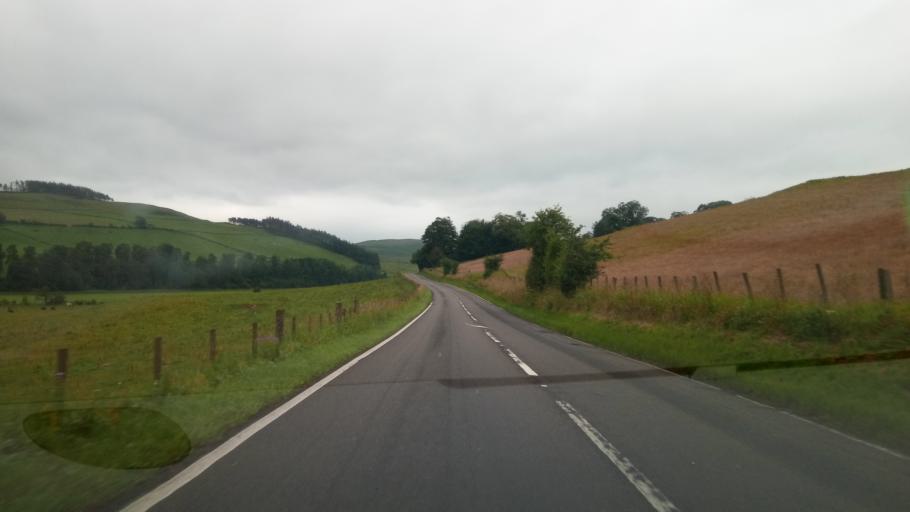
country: GB
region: Scotland
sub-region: The Scottish Borders
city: Hawick
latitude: 55.3704
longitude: -2.8792
